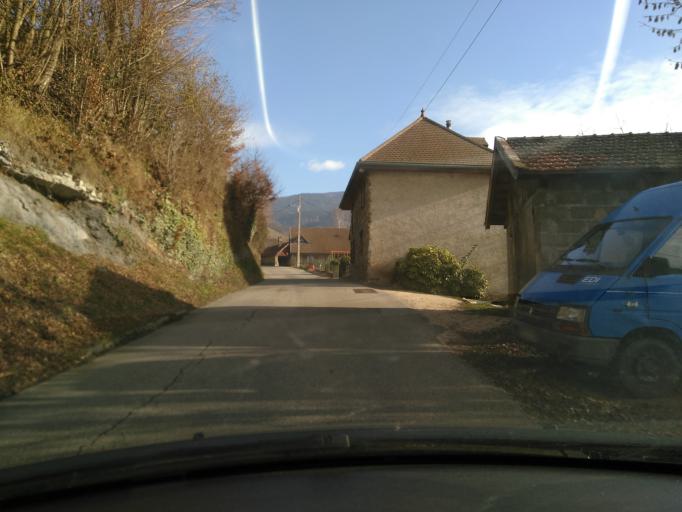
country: FR
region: Rhone-Alpes
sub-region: Departement de l'Isere
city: Villard-Bonnot
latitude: 45.2369
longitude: 5.9197
